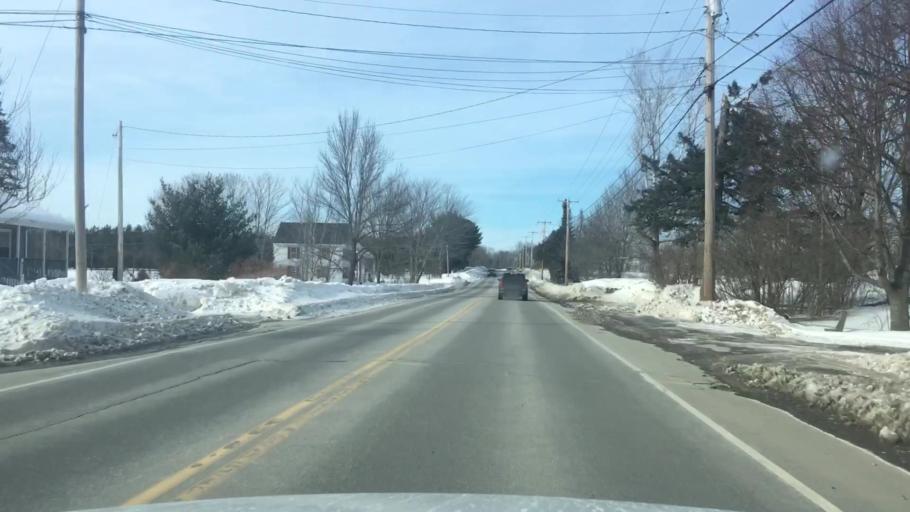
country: US
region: Maine
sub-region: Penobscot County
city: Kenduskeag
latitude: 44.9226
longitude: -68.9323
